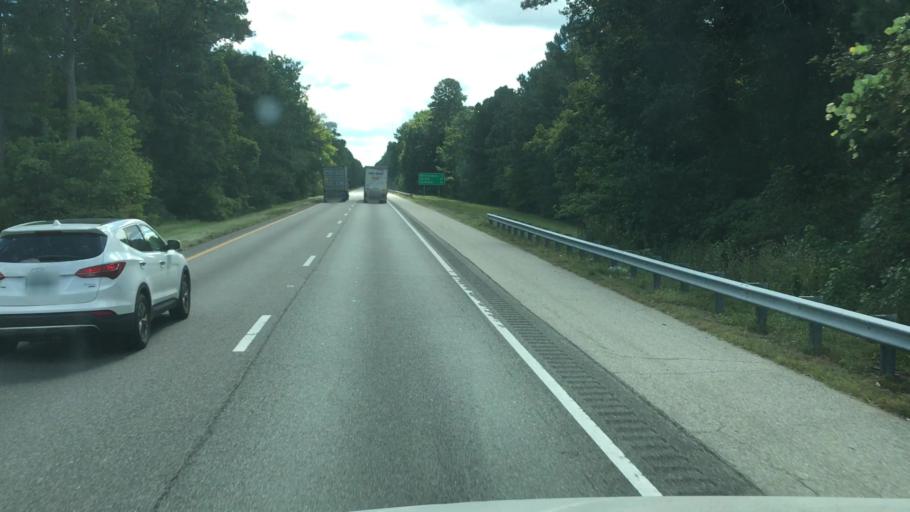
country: US
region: Virginia
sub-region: James City County
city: Williamsburg
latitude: 37.3436
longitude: -76.7215
